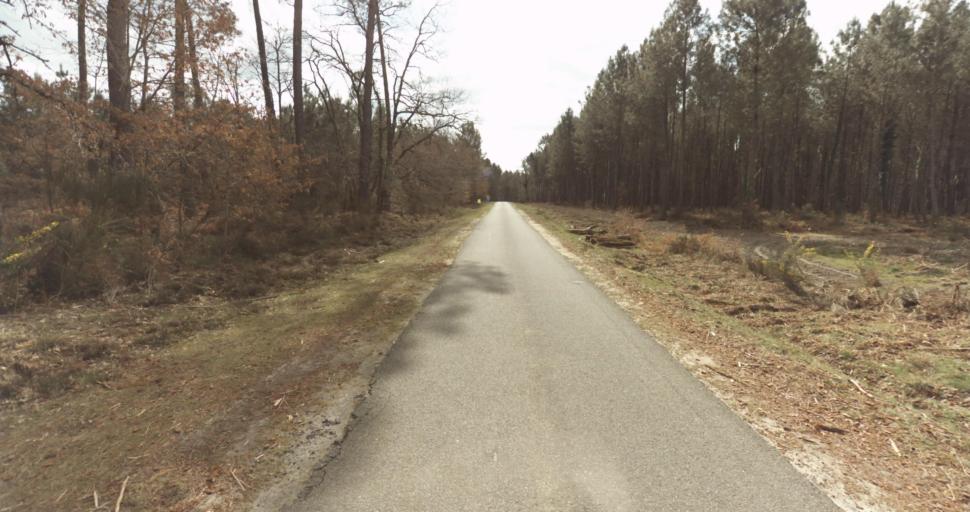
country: FR
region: Aquitaine
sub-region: Departement des Landes
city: Roquefort
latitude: 44.0496
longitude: -0.4254
